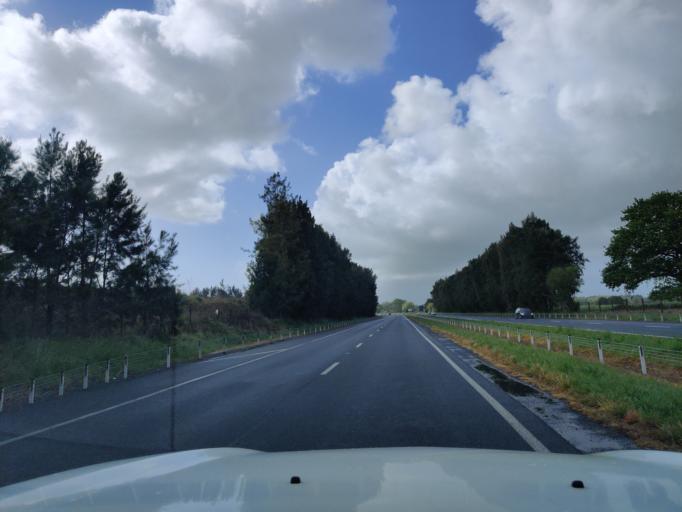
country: NZ
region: Waikato
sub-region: Waipa District
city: Cambridge
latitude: -37.8361
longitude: 175.3653
